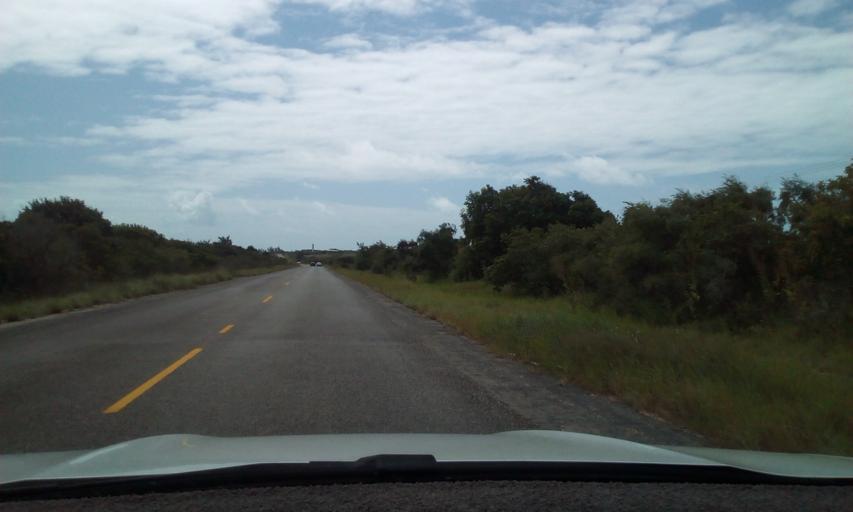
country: BR
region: Paraiba
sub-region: Rio Tinto
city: Rio Tinto
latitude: -6.7390
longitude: -34.9650
